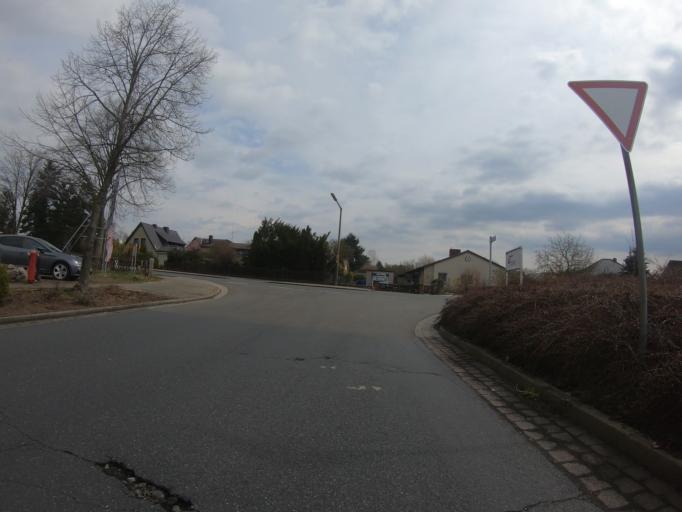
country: DE
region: Lower Saxony
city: Hankensbuttel
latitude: 52.7227
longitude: 10.5976
